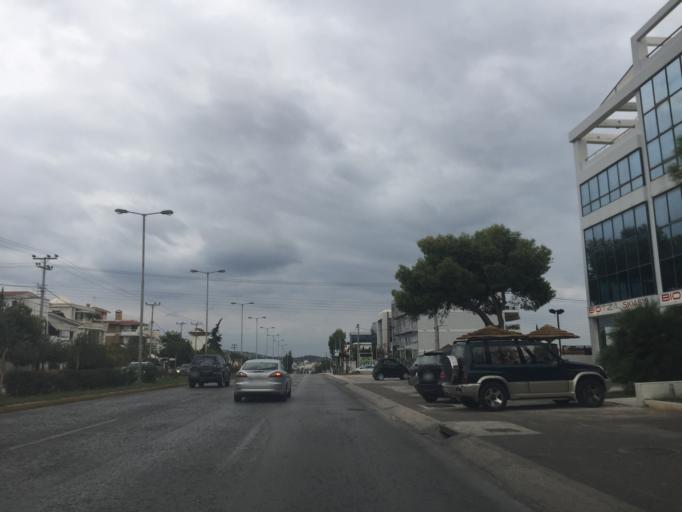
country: GR
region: Attica
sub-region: Nomarchia Anatolikis Attikis
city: Voula
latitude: 37.8492
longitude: 23.7685
